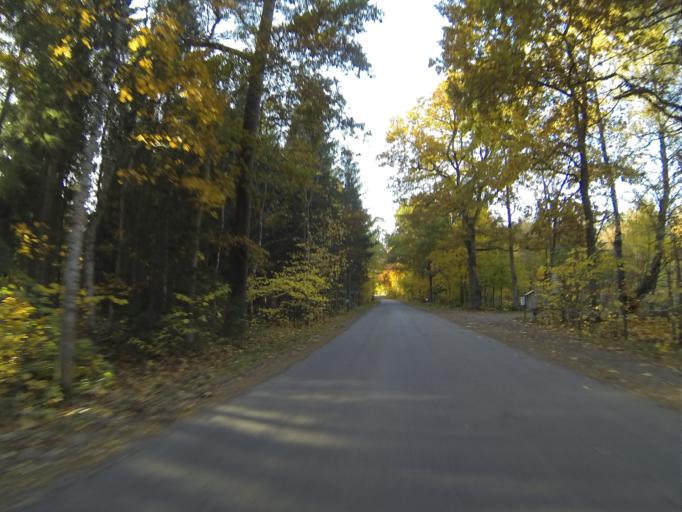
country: SE
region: Skane
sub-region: Lunds Kommun
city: Veberod
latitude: 55.6874
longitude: 13.4719
